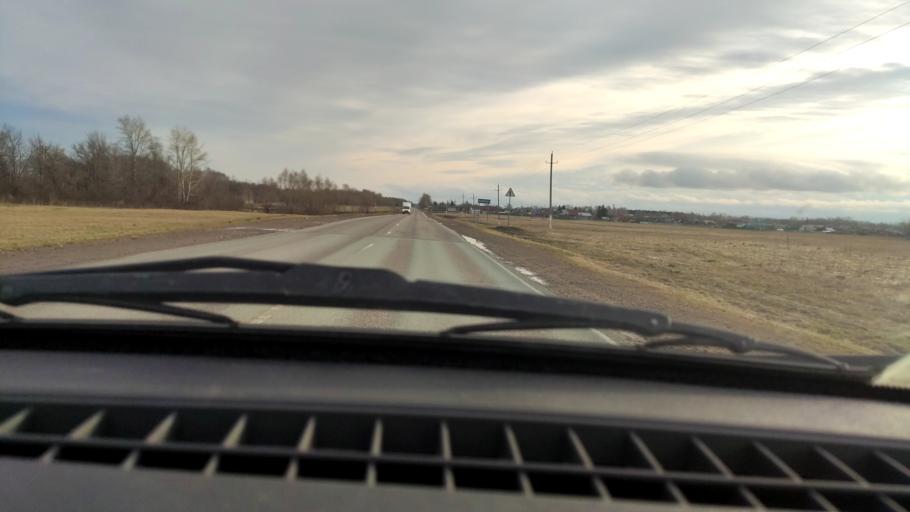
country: RU
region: Bashkortostan
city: Davlekanovo
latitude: 54.3041
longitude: 55.1362
